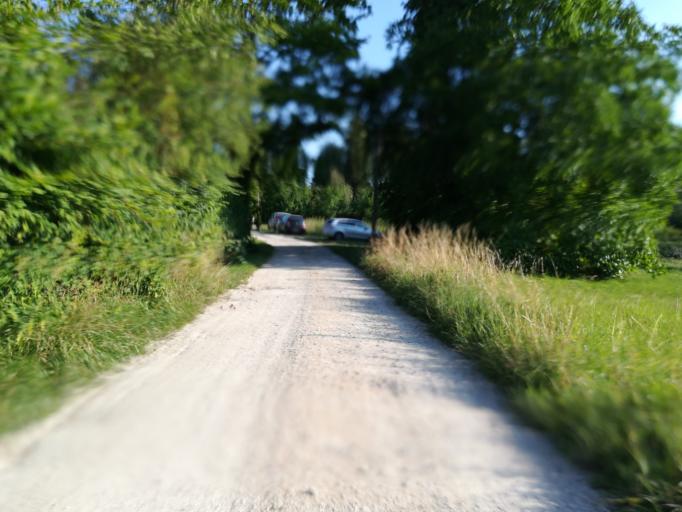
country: DE
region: Baden-Wuerttemberg
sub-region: Freiburg Region
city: Singen
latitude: 47.7558
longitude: 8.8239
